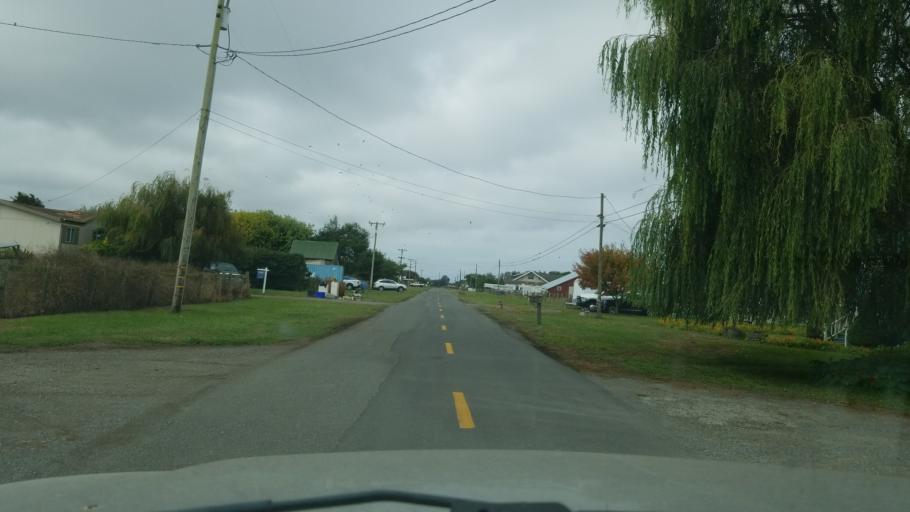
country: US
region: California
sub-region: Humboldt County
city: Ferndale
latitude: 40.5953
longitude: -124.2798
